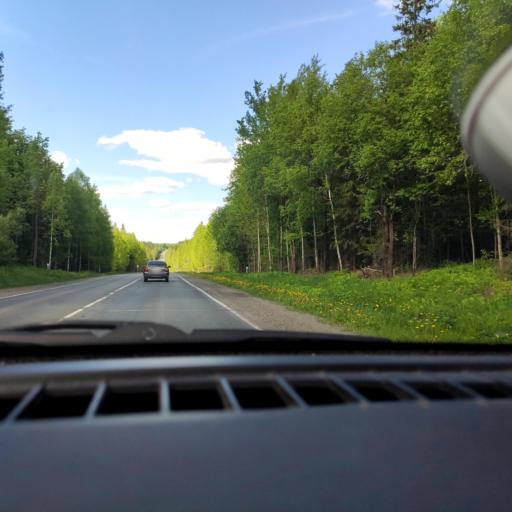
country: RU
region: Perm
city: Perm
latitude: 58.2260
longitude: 56.1639
